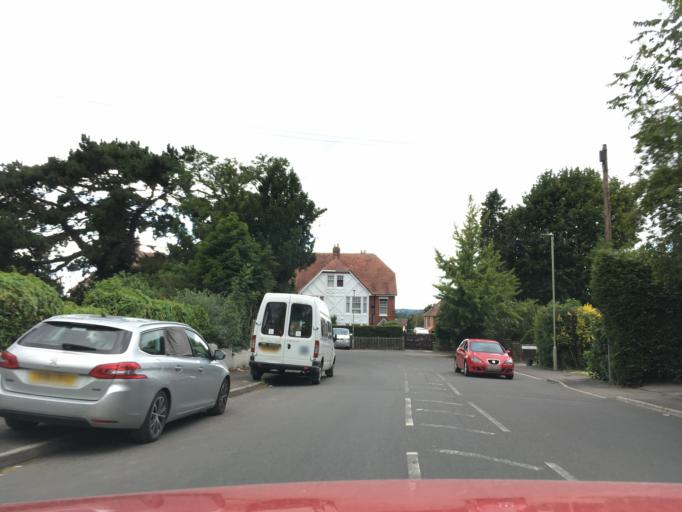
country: GB
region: England
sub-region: Gloucestershire
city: Gloucester
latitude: 51.8410
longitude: -2.2389
